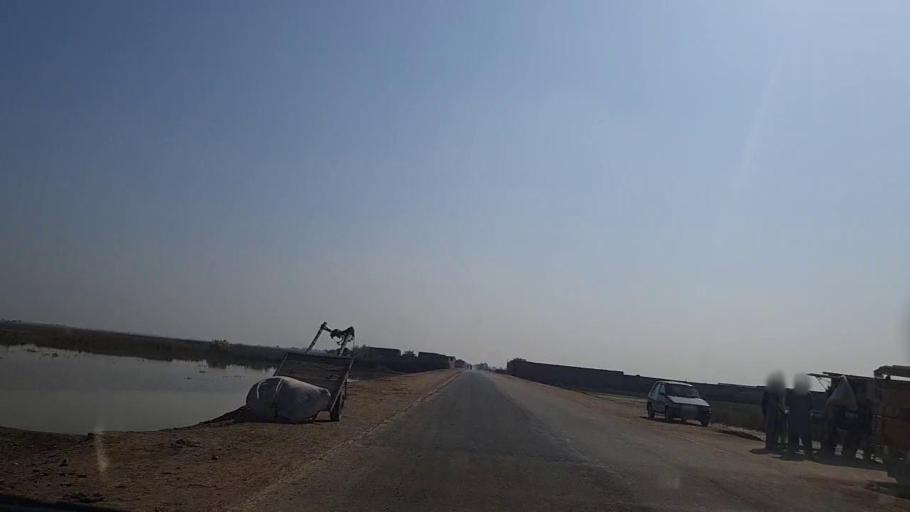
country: PK
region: Sindh
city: Sakrand
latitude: 26.0738
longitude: 68.4052
